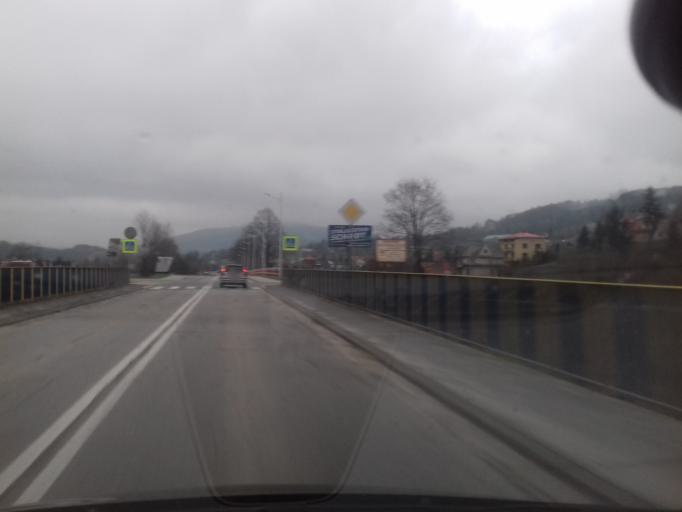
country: PL
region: Lesser Poland Voivodeship
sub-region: Powiat limanowski
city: Mszana Dolna
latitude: 49.6860
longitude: 20.0505
